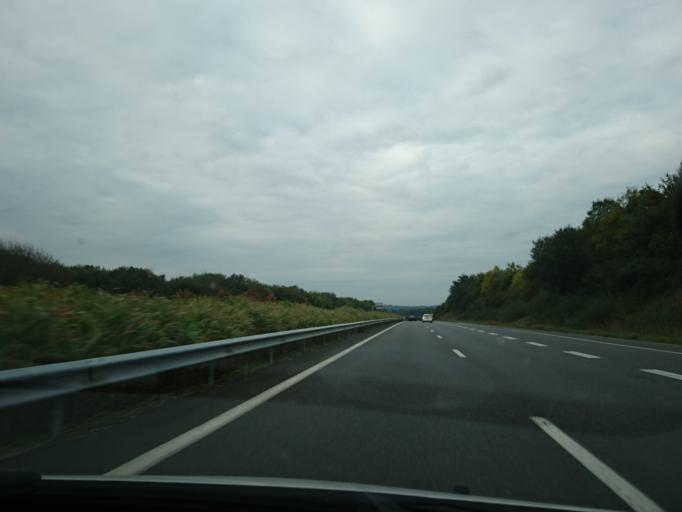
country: FR
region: Brittany
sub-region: Departement du Morbihan
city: Nivillac
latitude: 47.5218
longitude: -2.2812
